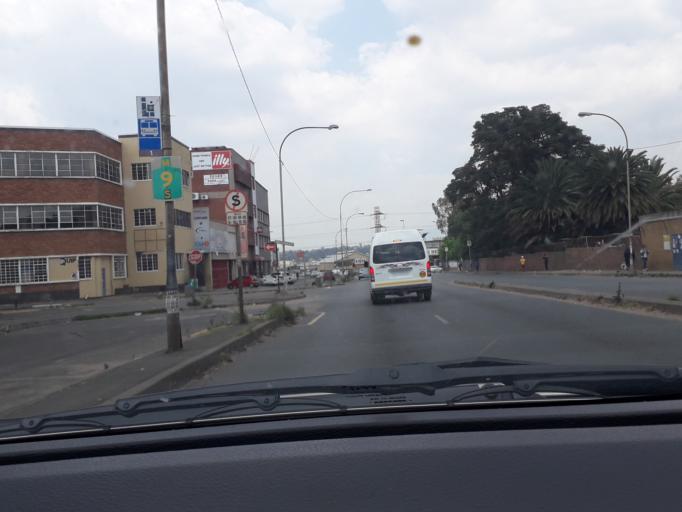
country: ZA
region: Gauteng
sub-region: City of Johannesburg Metropolitan Municipality
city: Johannesburg
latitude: -26.2218
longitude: 28.0436
